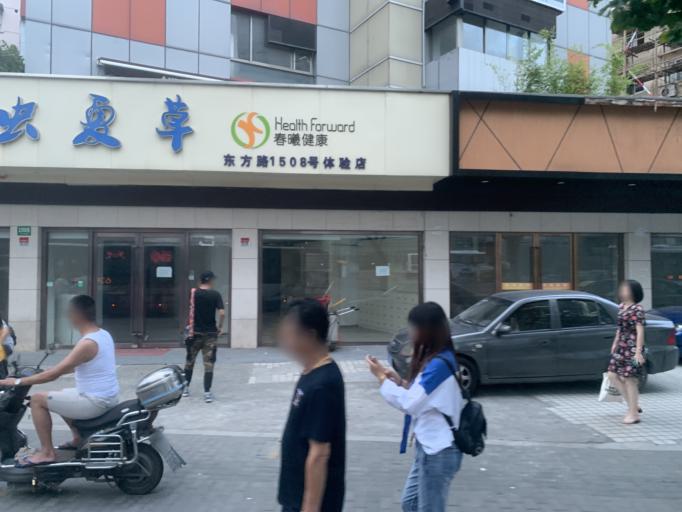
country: CN
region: Shanghai Shi
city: Huamu
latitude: 31.2129
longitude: 121.5228
